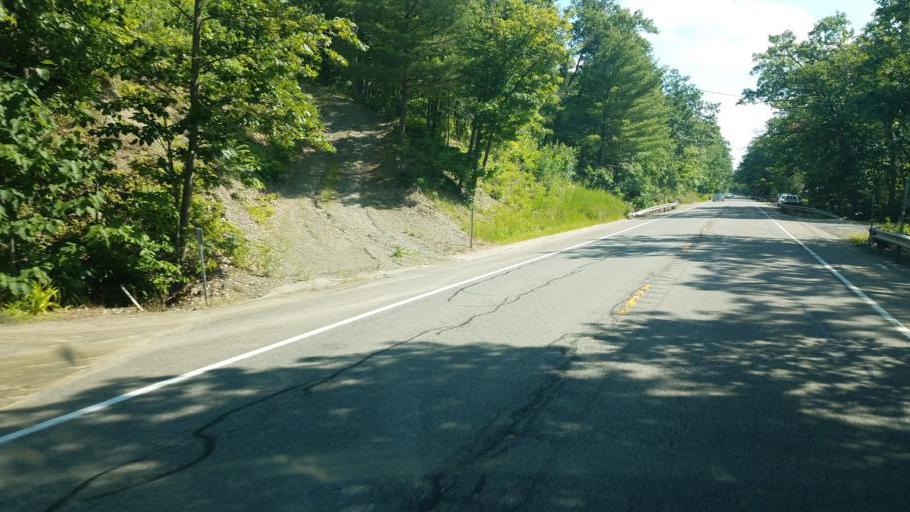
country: US
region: New York
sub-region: Steuben County
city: Sylvan Beach
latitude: 42.4591
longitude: -77.1631
